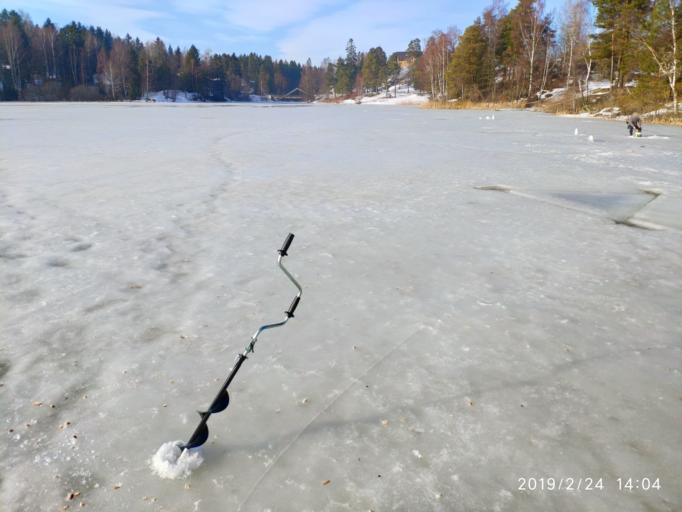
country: NO
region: Akershus
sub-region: Lorenskog
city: Kjenn
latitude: 59.9314
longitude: 10.9665
